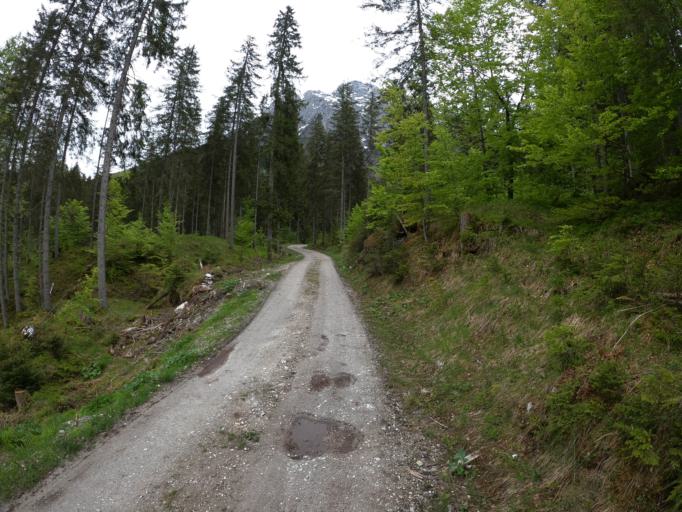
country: AT
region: Salzburg
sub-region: Politischer Bezirk Sankt Johann im Pongau
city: Werfen
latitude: 47.4724
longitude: 13.0796
